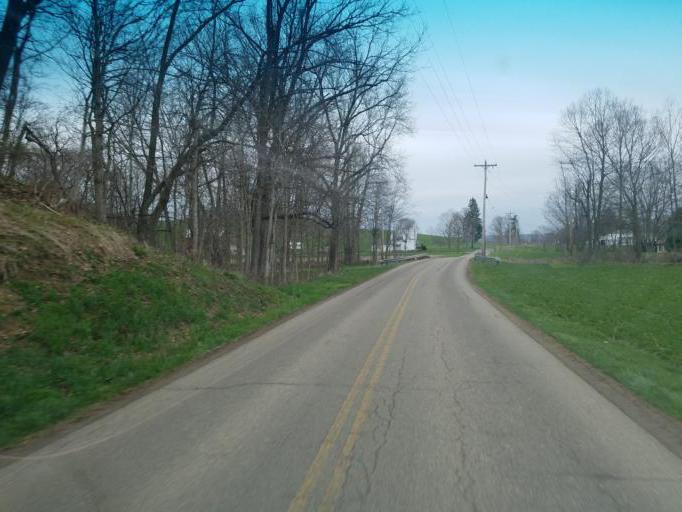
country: US
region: Ohio
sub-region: Holmes County
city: Millersburg
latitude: 40.6160
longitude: -81.9447
